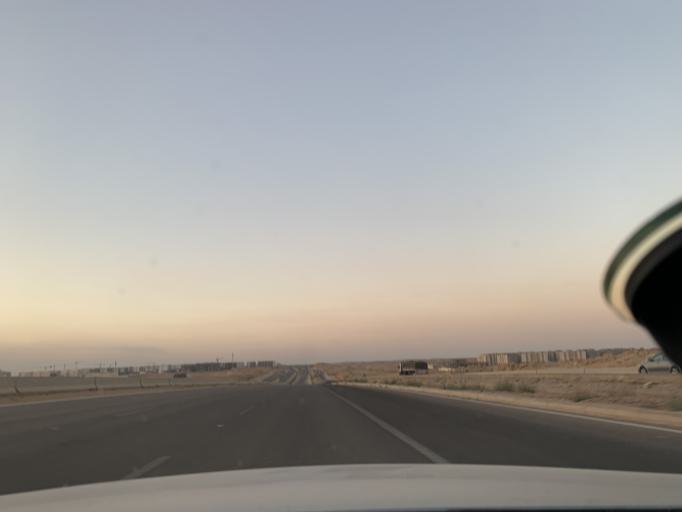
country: EG
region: Muhafazat al Qahirah
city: Halwan
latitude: 29.9546
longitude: 31.5413
